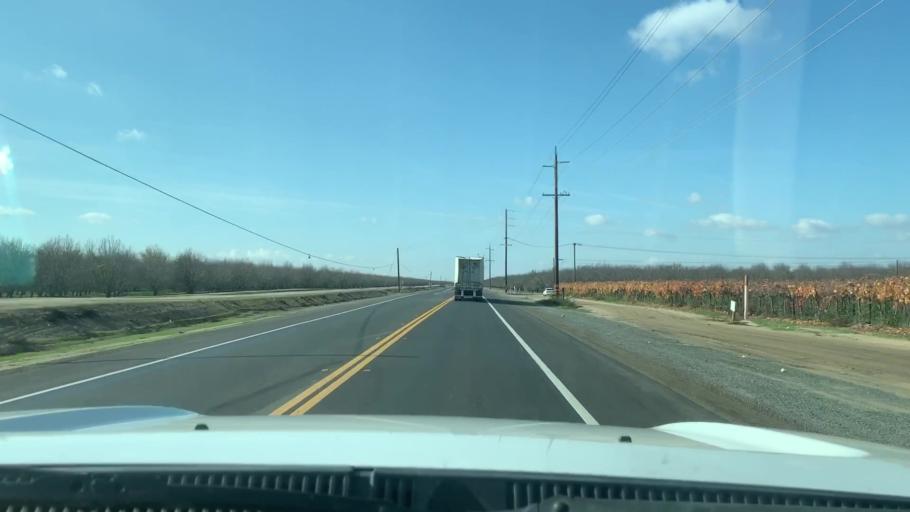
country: US
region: California
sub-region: Kern County
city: Wasco
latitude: 35.6018
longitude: -119.2752
